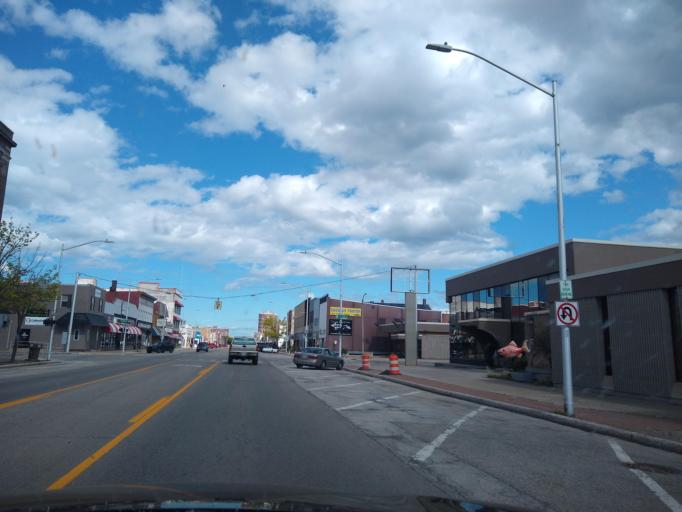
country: US
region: Michigan
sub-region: Delta County
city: Escanaba
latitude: 45.7457
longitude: -87.0650
